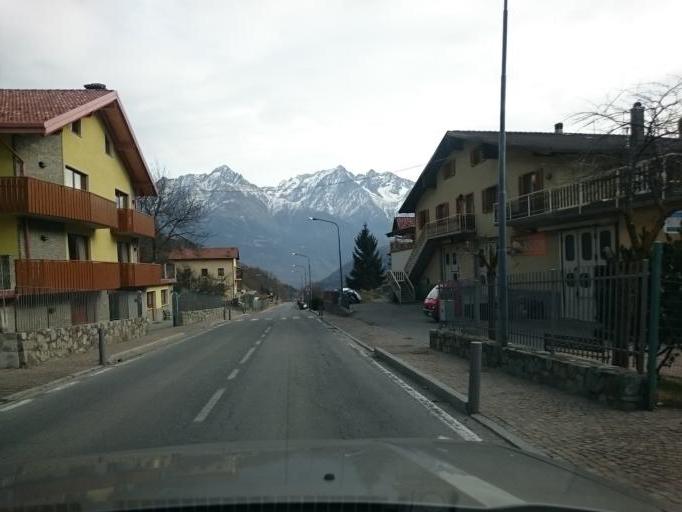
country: IT
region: Lombardy
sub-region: Provincia di Brescia
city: Corteno Golgi
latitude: 46.1732
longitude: 10.2777
